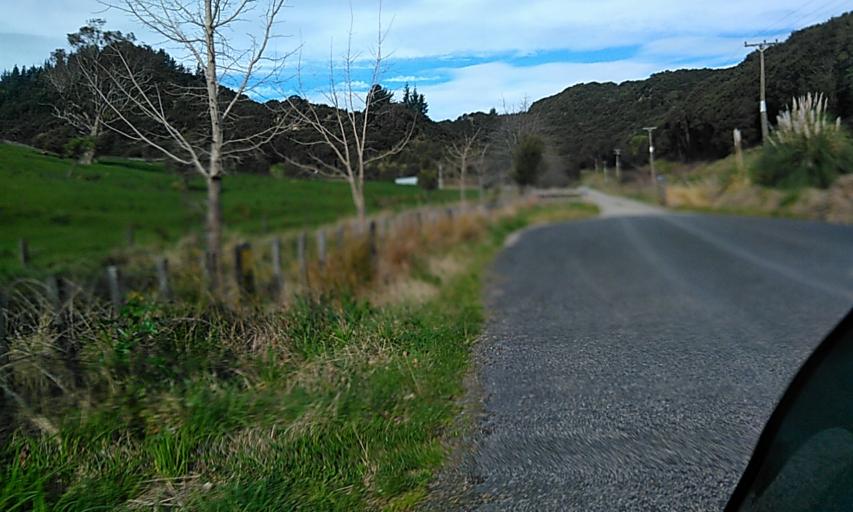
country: NZ
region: Gisborne
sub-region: Gisborne District
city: Gisborne
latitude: -38.6131
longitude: 178.0245
